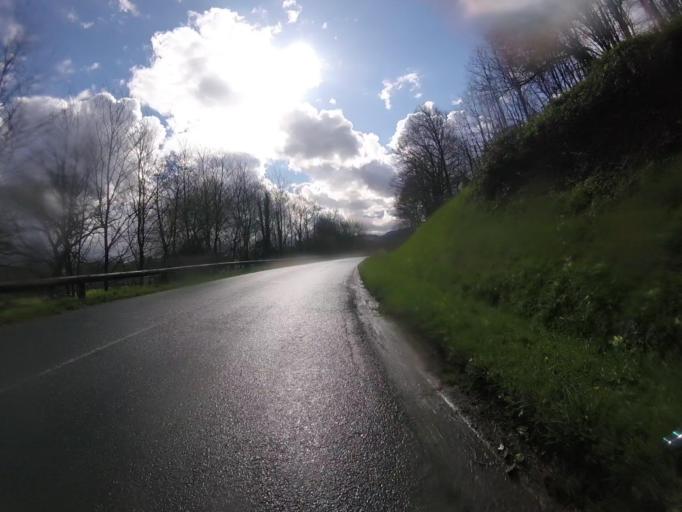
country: FR
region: Aquitaine
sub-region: Departement des Pyrenees-Atlantiques
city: Sare
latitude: 43.3135
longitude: -1.5750
